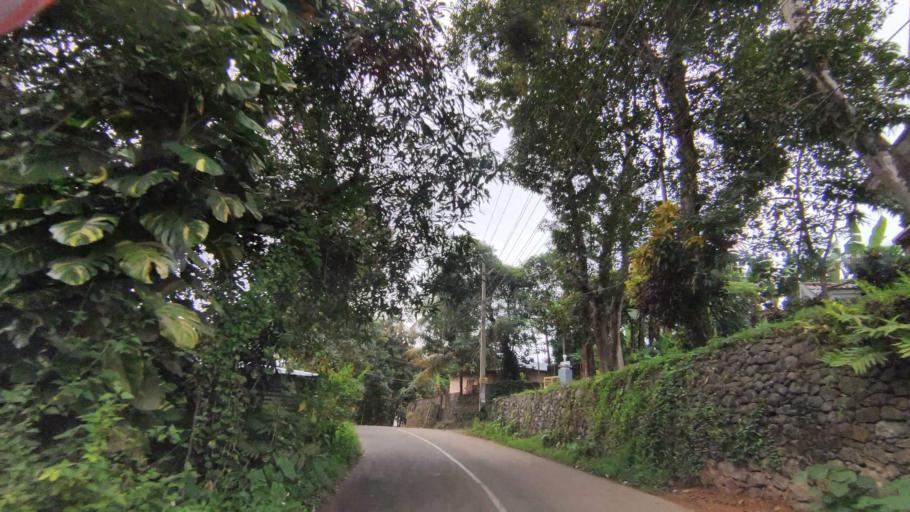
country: IN
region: Kerala
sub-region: Kottayam
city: Kottayam
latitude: 9.6425
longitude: 76.5177
